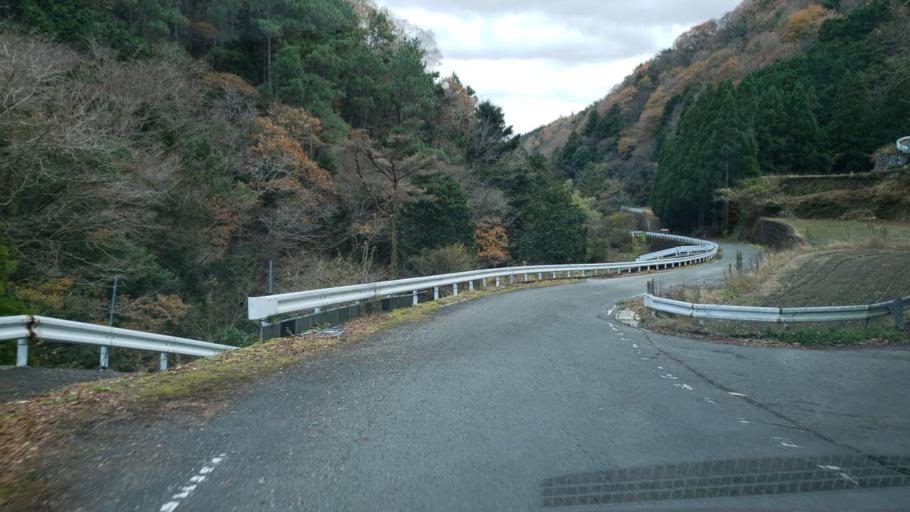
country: JP
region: Tokushima
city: Wakimachi
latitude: 34.1486
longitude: 134.2280
